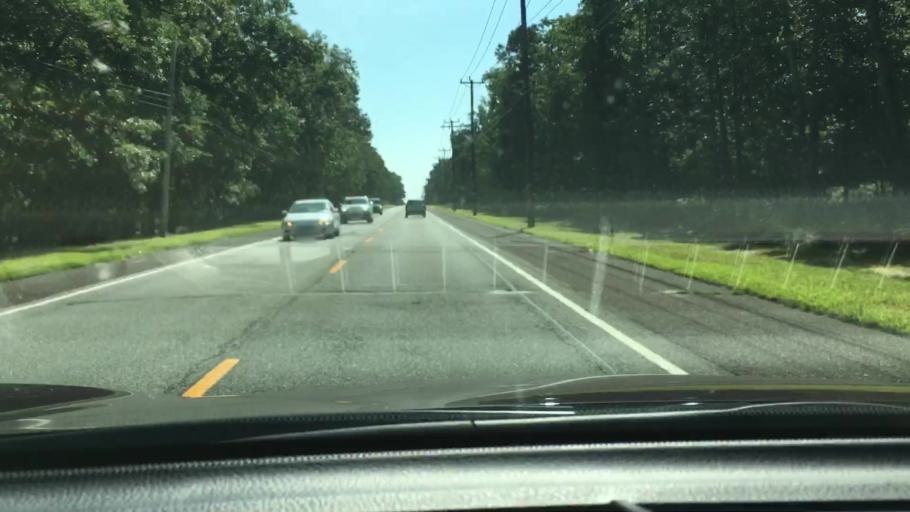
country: US
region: New Jersey
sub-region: Cumberland County
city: Millville
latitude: 39.3826
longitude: -74.9762
